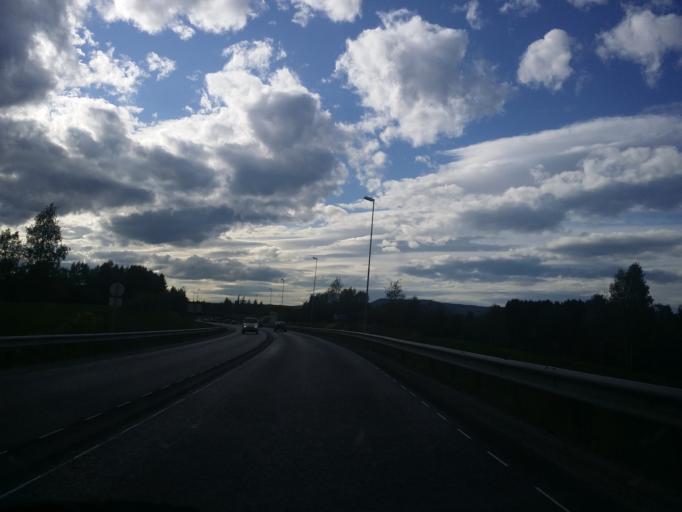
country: NO
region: Hedmark
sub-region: Hamar
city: Hamar
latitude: 60.8308
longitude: 11.0858
